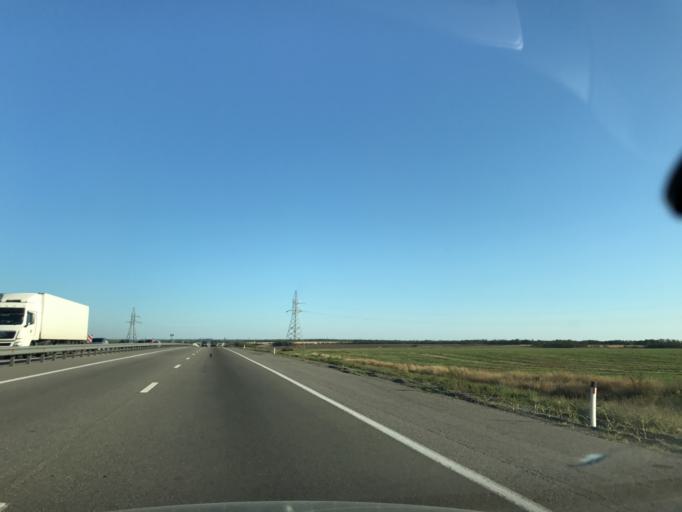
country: RU
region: Rostov
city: Zverevo
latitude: 47.9566
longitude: 40.2179
